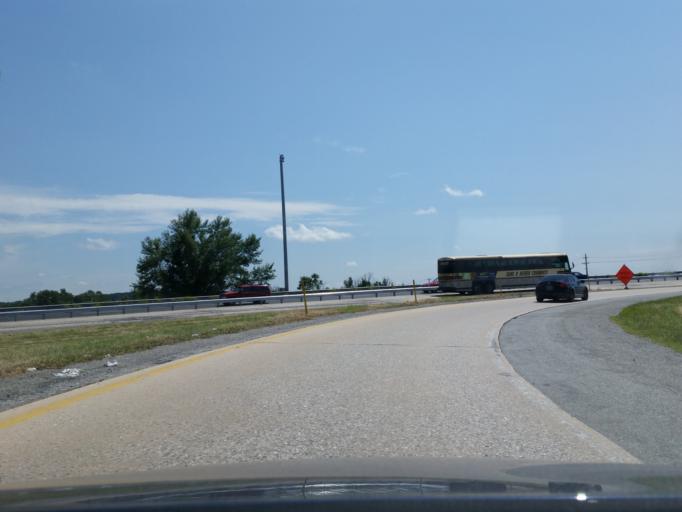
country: US
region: Pennsylvania
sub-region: York County
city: Yorklyn
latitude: 39.9873
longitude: -76.6663
